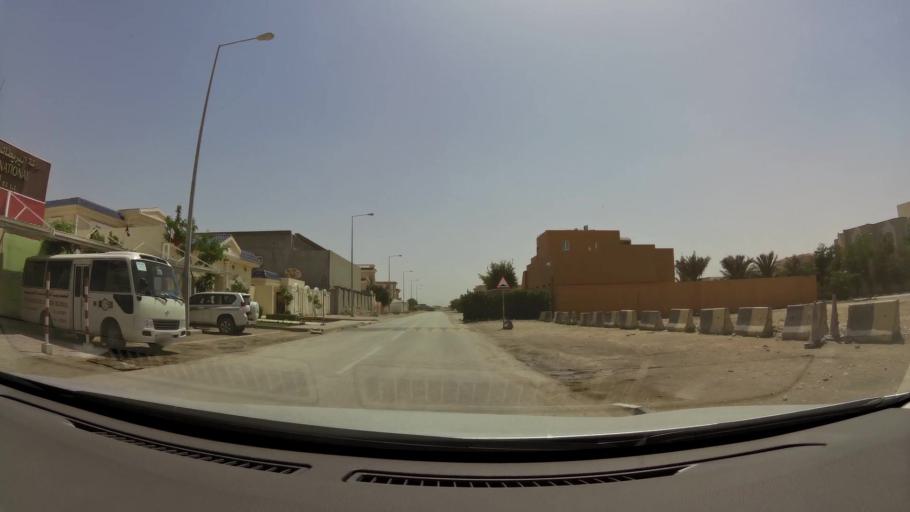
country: QA
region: Baladiyat Umm Salal
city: Umm Salal Muhammad
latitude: 25.3897
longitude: 51.4528
